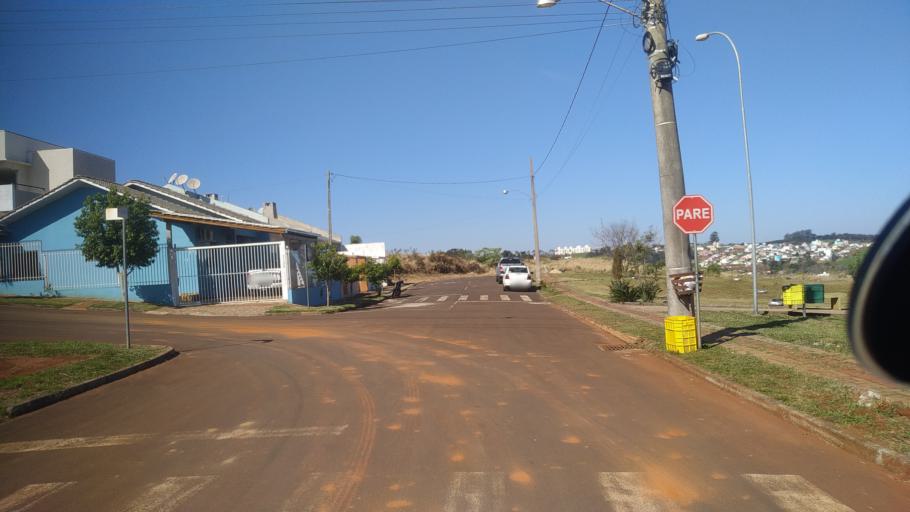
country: BR
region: Santa Catarina
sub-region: Chapeco
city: Chapeco
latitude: -27.0900
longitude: -52.5819
